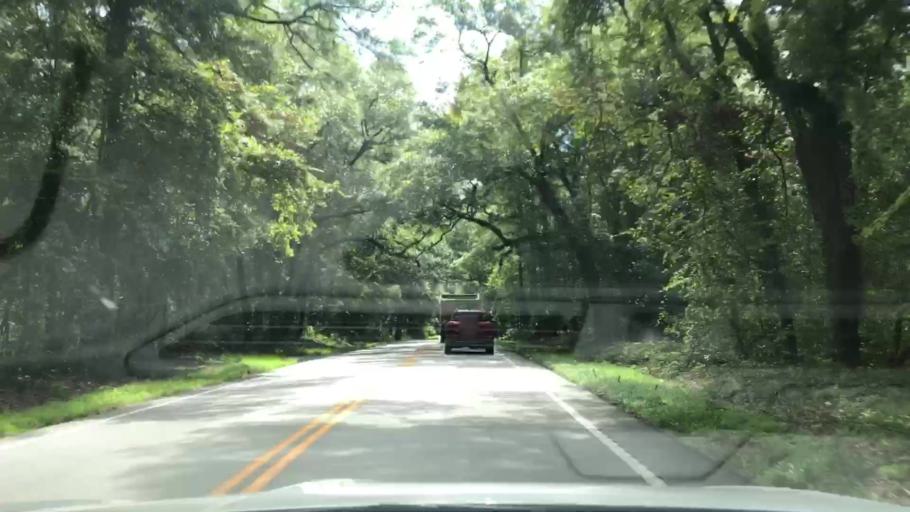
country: US
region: South Carolina
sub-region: Berkeley County
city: Ladson
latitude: 32.8893
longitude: -80.1242
